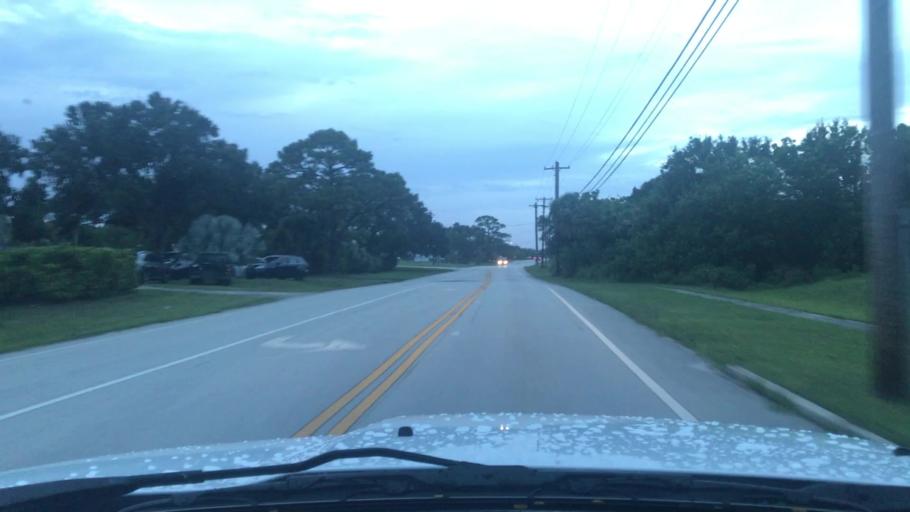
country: US
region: Florida
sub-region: Indian River County
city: Florida Ridge
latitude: 27.5969
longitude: -80.3841
